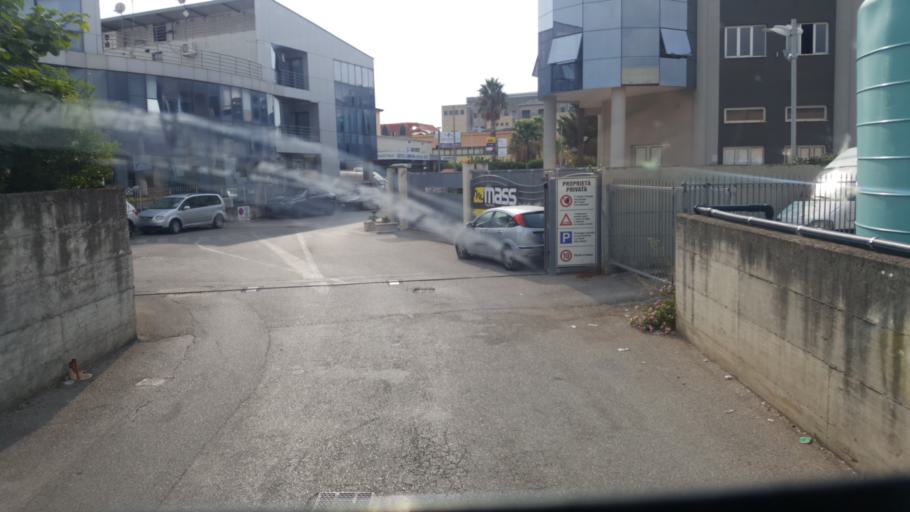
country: IT
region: Campania
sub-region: Provincia di Salerno
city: Battipaglia
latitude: 40.5983
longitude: 14.9864
